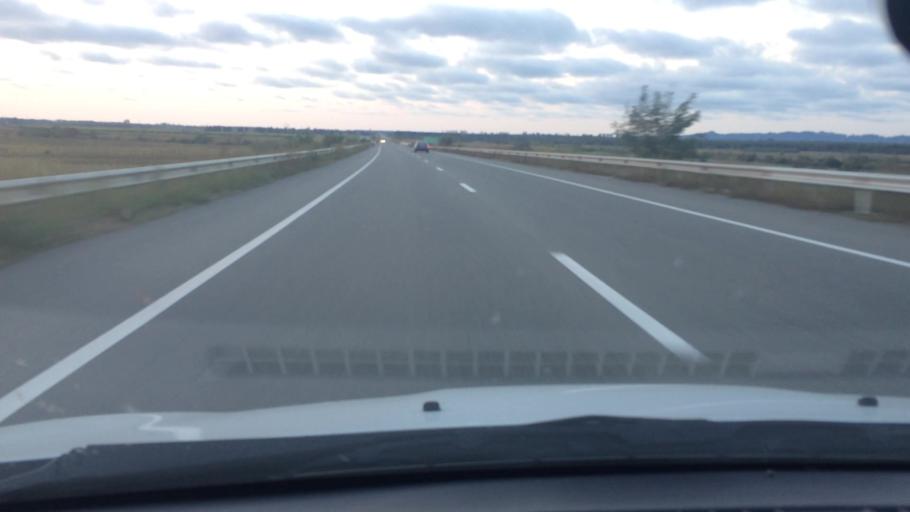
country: GE
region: Ajaria
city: Ochkhamuri
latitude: 41.8687
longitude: 41.8331
